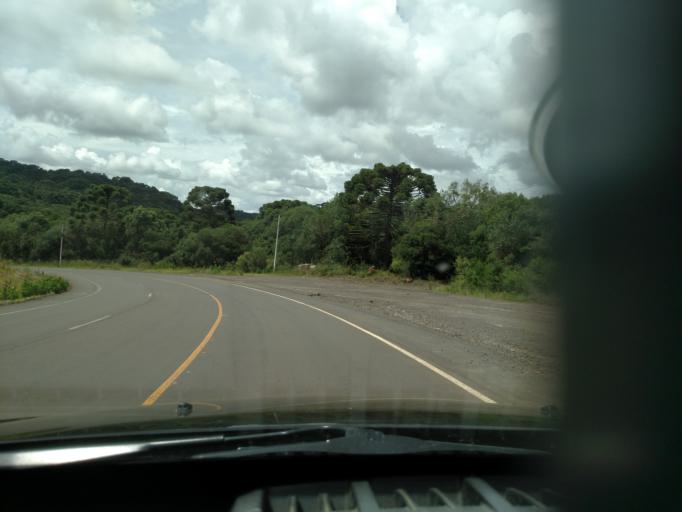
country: BR
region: Rio Grande do Sul
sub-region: Vacaria
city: Estrela
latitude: -27.9224
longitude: -50.6408
